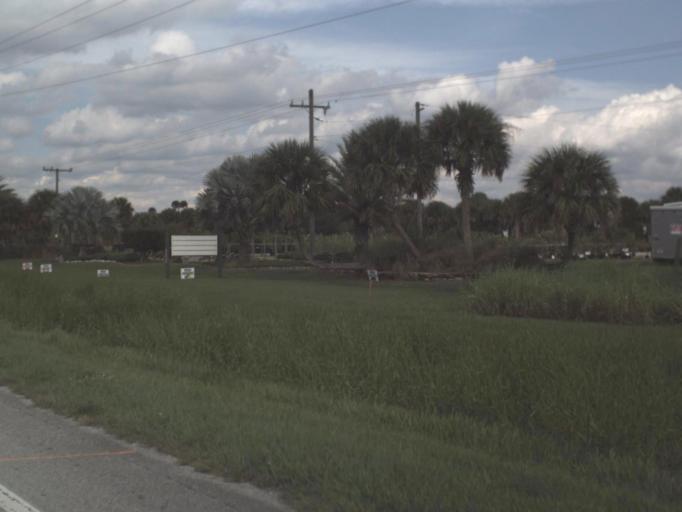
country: US
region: Florida
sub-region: Okeechobee County
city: Cypress Quarters
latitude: 27.3914
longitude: -80.8159
